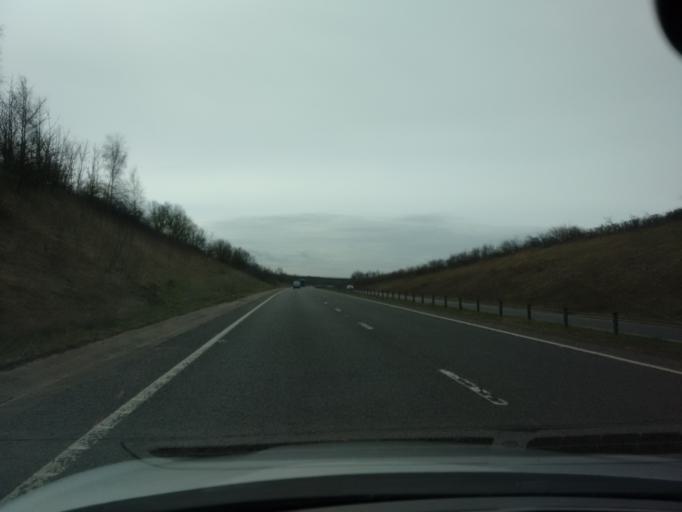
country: GB
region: England
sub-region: Warwickshire
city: Bidford-on-avon
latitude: 52.1817
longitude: -1.8784
